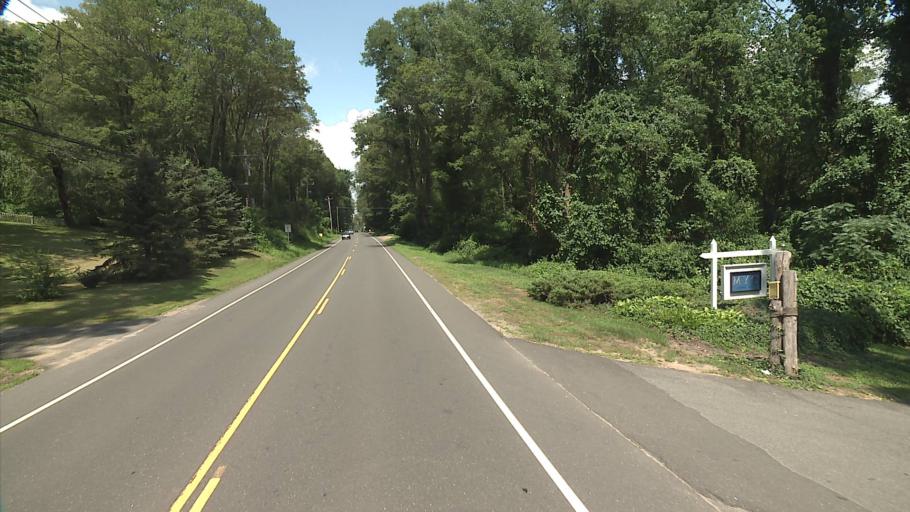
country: US
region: Connecticut
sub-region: Middlesex County
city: East Haddam
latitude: 41.4306
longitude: -72.4530
